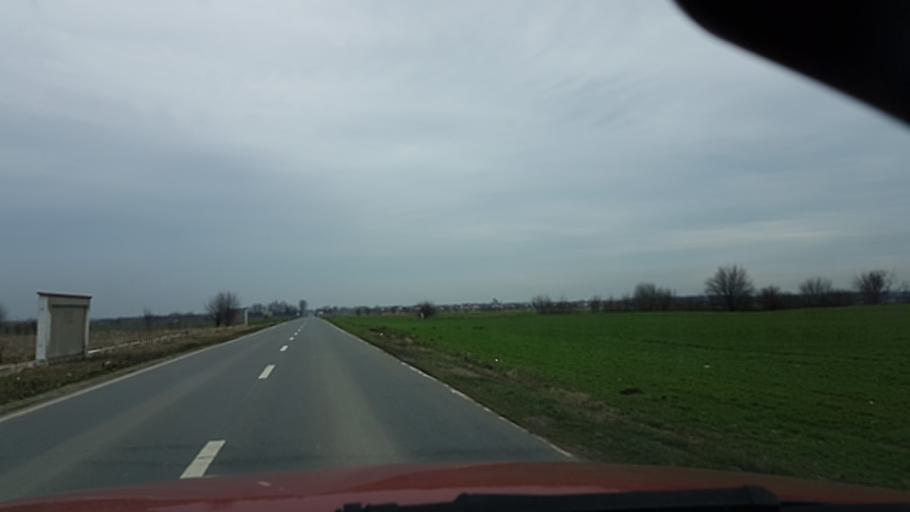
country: RO
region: Ilfov
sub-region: Comuna Tunari
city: Tunari
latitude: 44.5678
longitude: 26.1410
